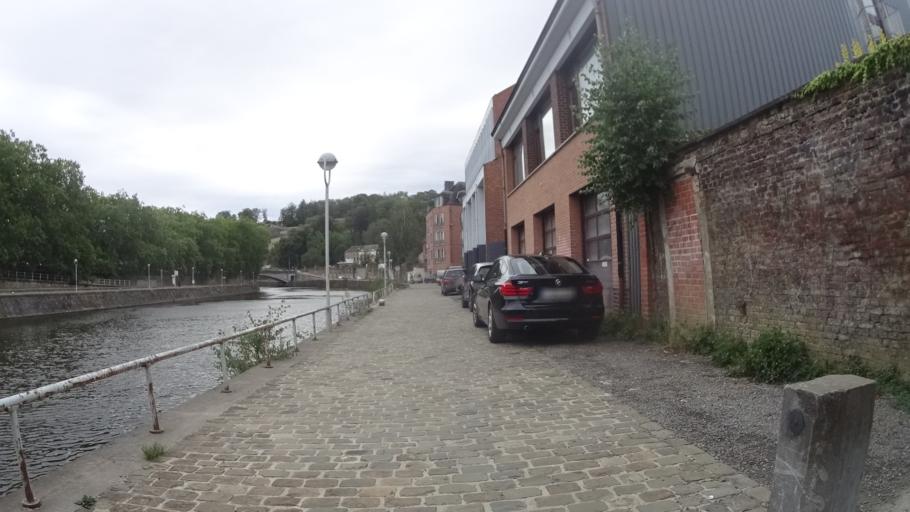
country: BE
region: Wallonia
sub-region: Province de Namur
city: Namur
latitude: 50.4642
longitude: 4.8557
